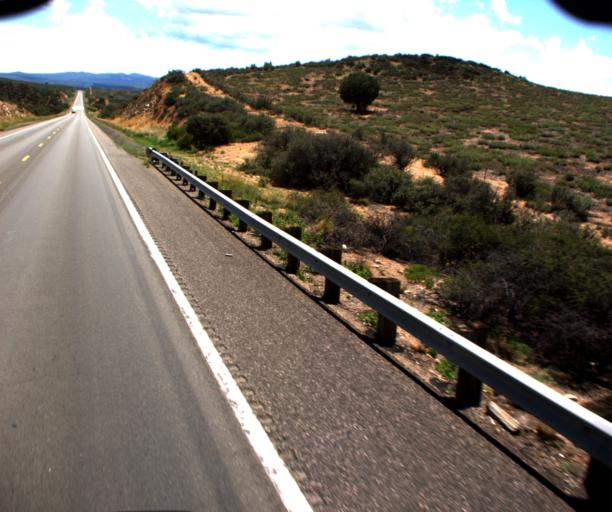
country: US
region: Arizona
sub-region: Yavapai County
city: Dewey-Humboldt
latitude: 34.5320
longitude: -112.1210
